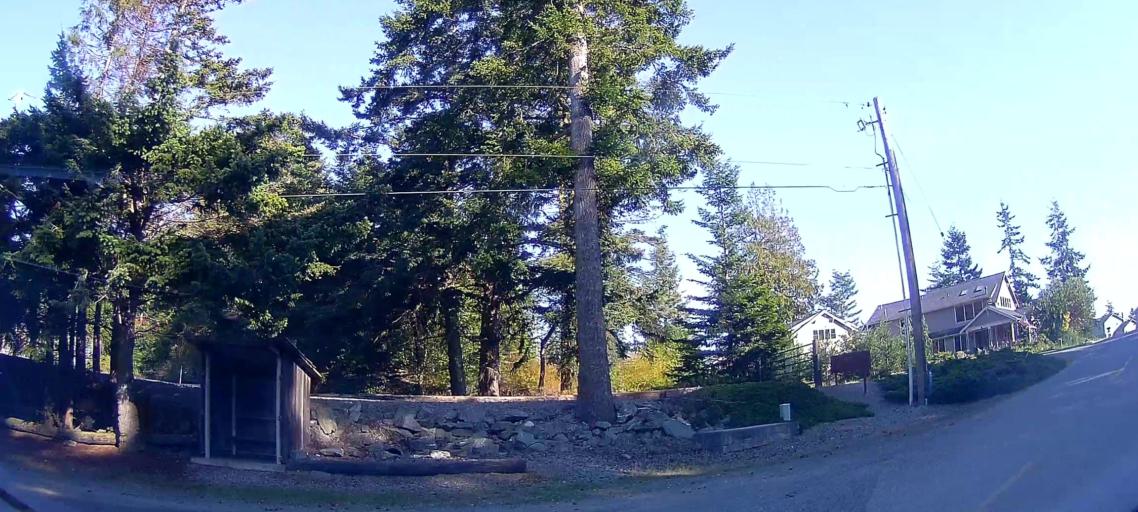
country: US
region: Washington
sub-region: Skagit County
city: Anacortes
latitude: 48.4983
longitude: -122.6879
